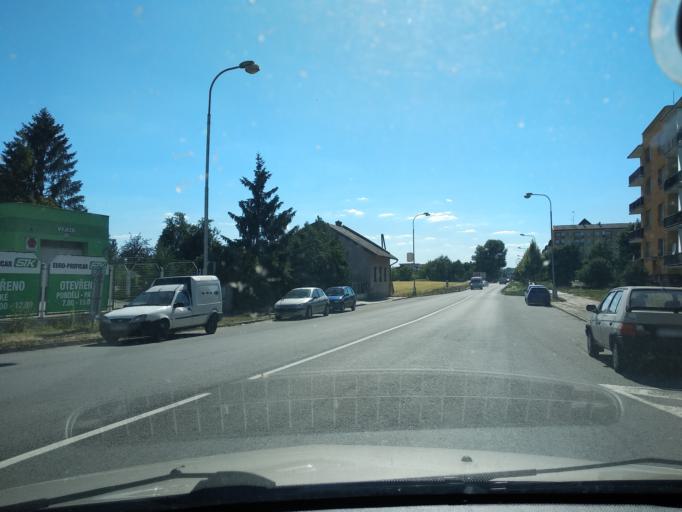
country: CZ
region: Olomoucky
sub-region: Okres Olomouc
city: Olomouc
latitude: 49.5711
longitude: 17.2595
